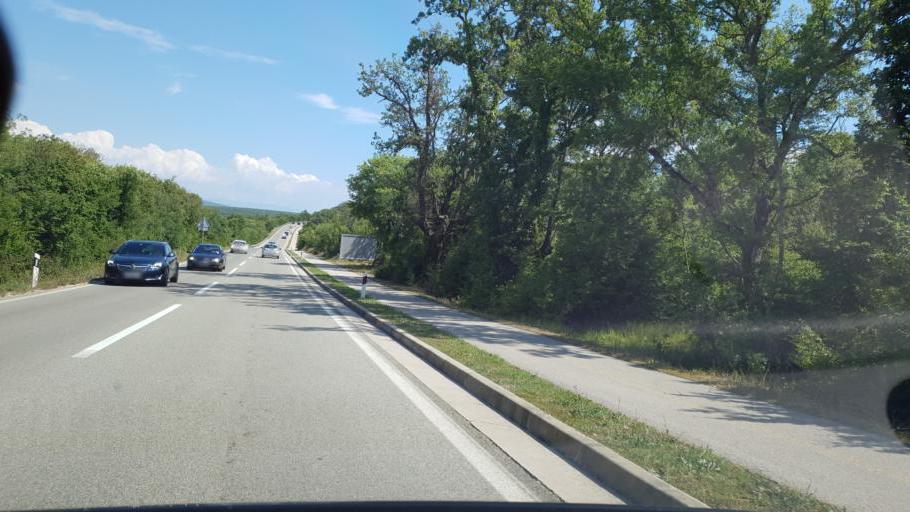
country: HR
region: Primorsko-Goranska
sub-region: Grad Krk
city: Krk
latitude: 45.0720
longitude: 14.5515
